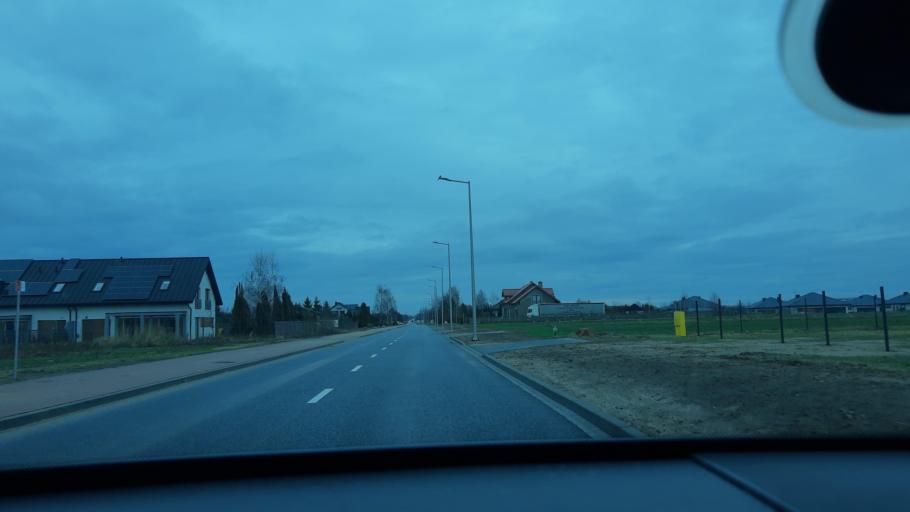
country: PL
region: Lodz Voivodeship
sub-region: Powiat sieradzki
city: Sieradz
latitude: 51.5852
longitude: 18.6849
